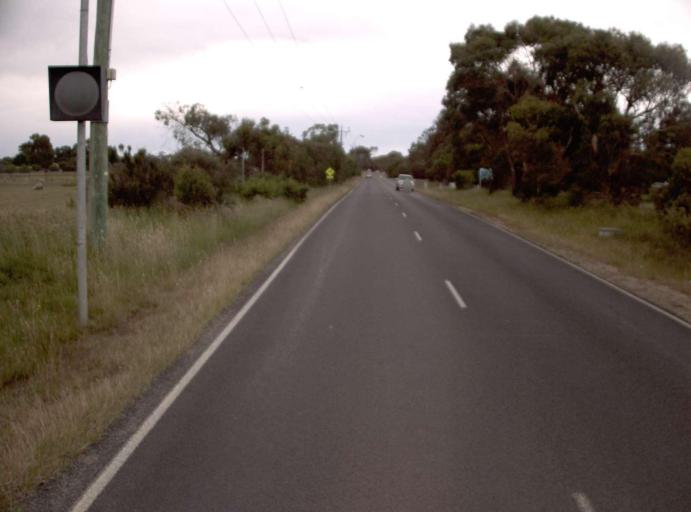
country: AU
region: Victoria
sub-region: Bass Coast
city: North Wonthaggi
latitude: -38.4318
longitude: 145.4918
